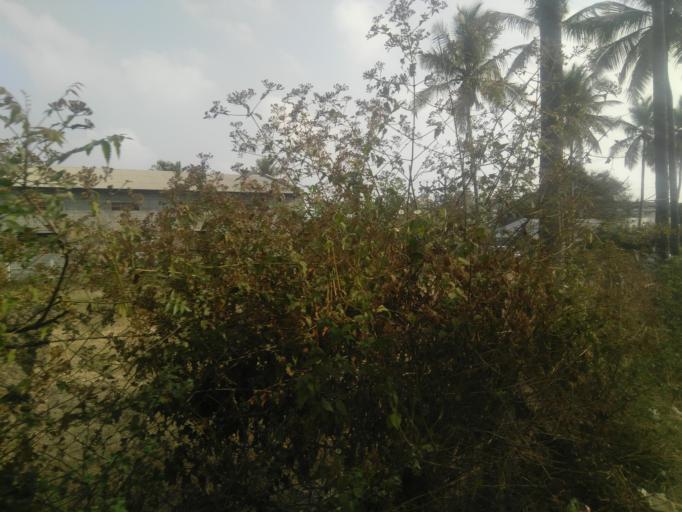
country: IN
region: Tamil Nadu
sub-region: Coimbatore
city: Periyanayakkanpalaiyam
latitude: 11.0774
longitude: 76.9241
